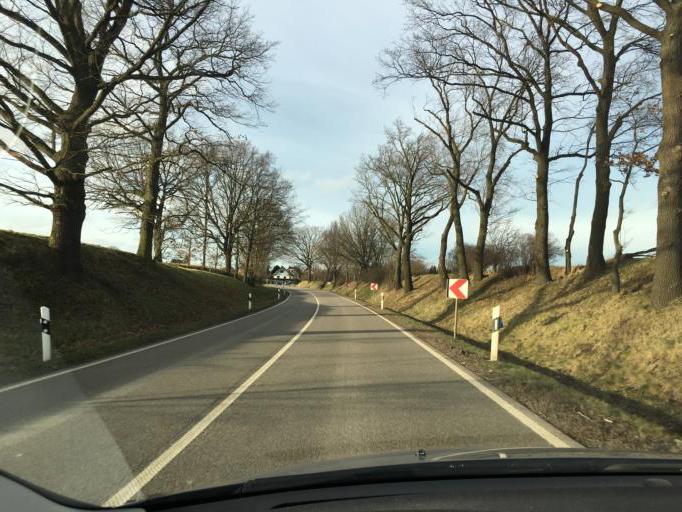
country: DE
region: Thuringia
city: Nobitz
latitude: 50.9670
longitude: 12.5005
